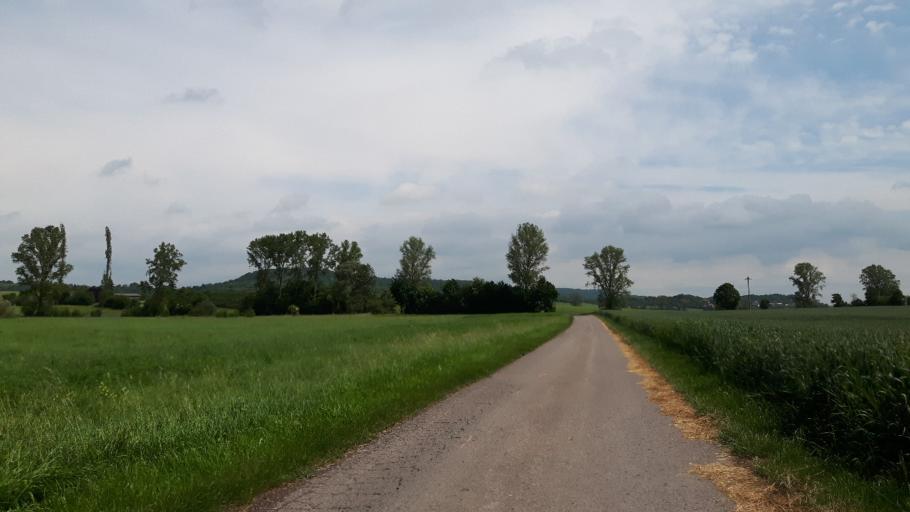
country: DE
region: Bavaria
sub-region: Regierungsbezirk Unterfranken
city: Herbstadt
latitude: 50.3042
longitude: 10.4983
